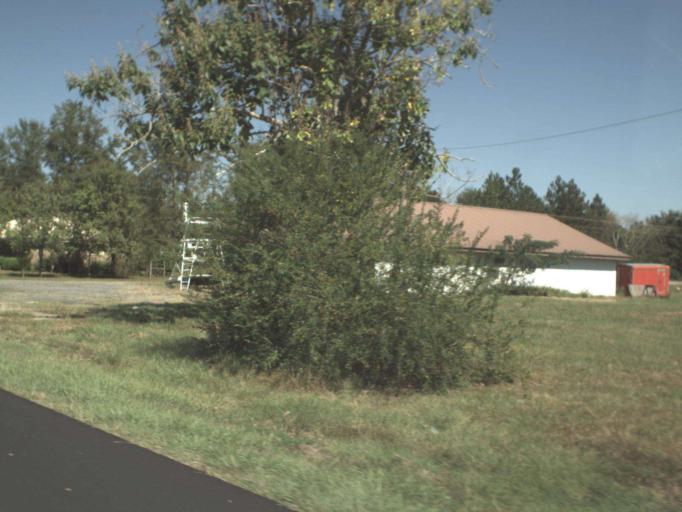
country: US
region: Alabama
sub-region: Covington County
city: Florala
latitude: 30.9437
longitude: -86.2835
